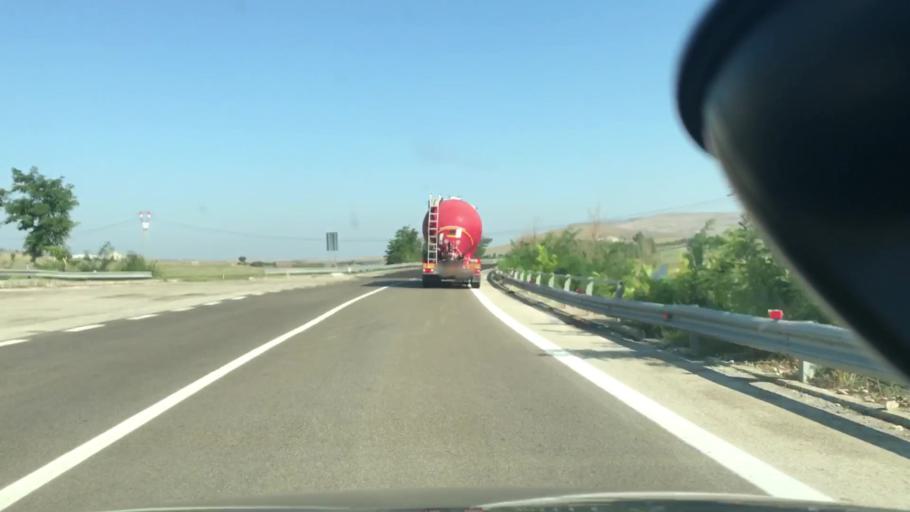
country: IT
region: Basilicate
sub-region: Provincia di Matera
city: Irsina
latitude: 40.7960
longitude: 16.2759
